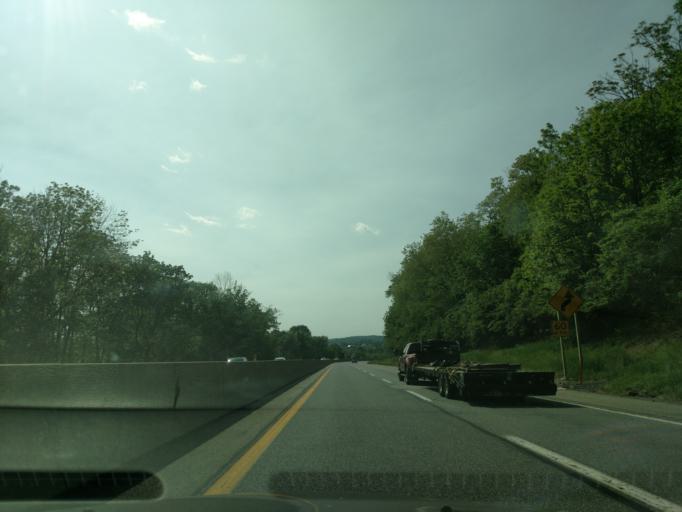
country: US
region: Pennsylvania
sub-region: Lancaster County
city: Denver
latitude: 40.2307
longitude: -76.1231
